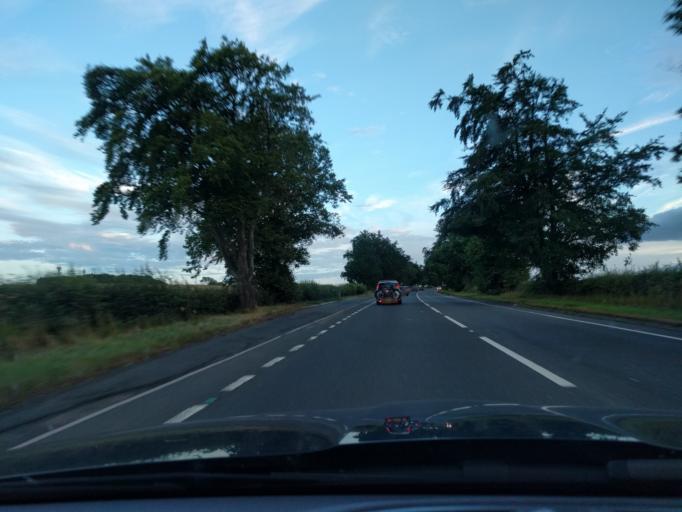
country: GB
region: England
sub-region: Northumberland
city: Hebron
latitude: 55.2115
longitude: -1.7101
